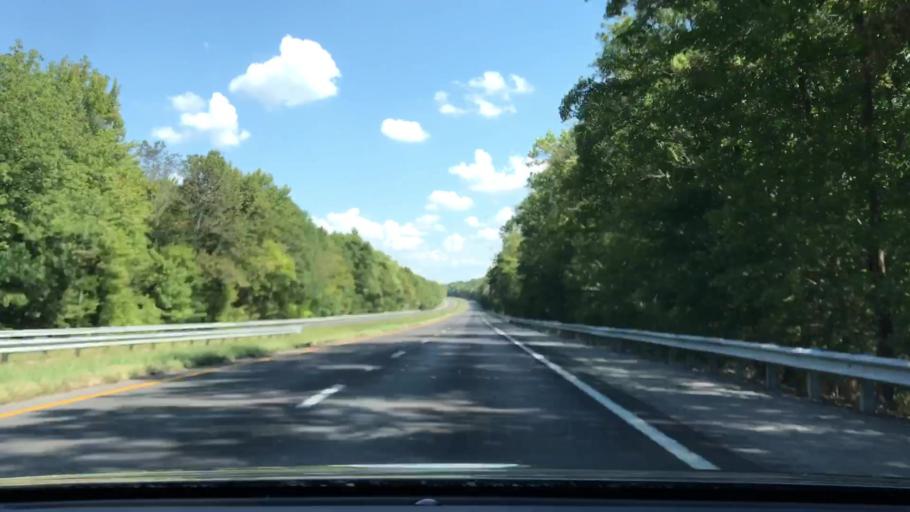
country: US
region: Kentucky
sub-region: Fulton County
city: Fulton
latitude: 36.5969
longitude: -88.8055
